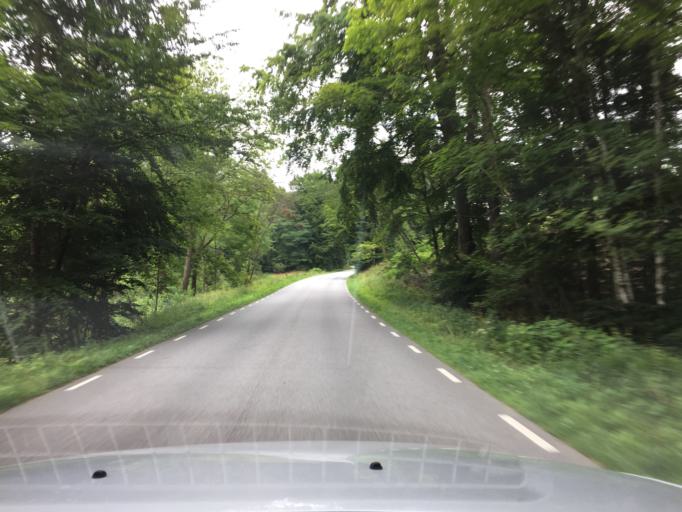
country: SE
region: Skane
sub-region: Hassleholms Kommun
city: Sosdala
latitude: 56.0483
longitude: 13.6512
